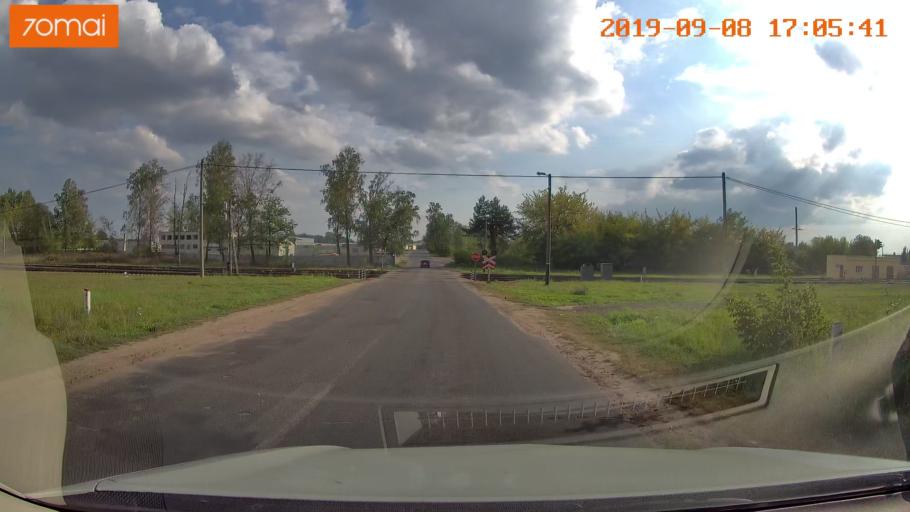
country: BY
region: Grodnenskaya
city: Hrodna
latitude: 53.6756
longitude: 23.9535
